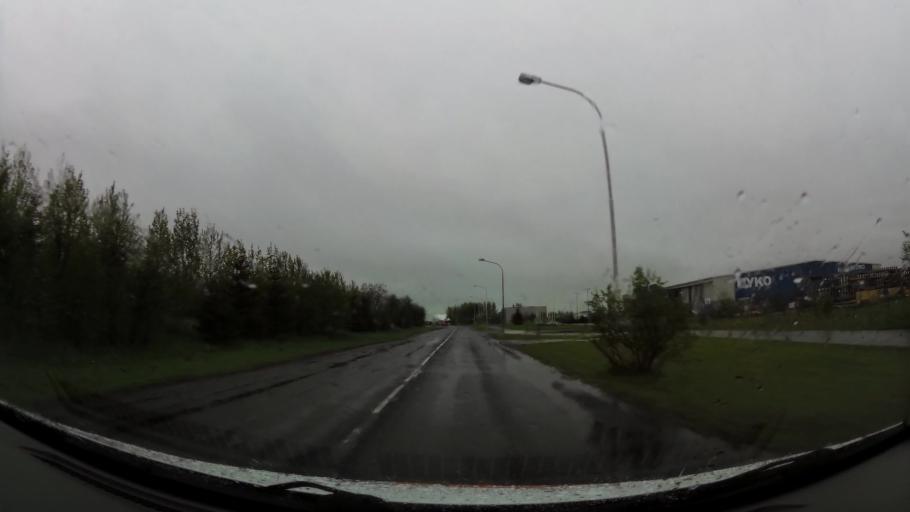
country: IS
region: South
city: Selfoss
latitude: 63.9362
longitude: -20.9788
